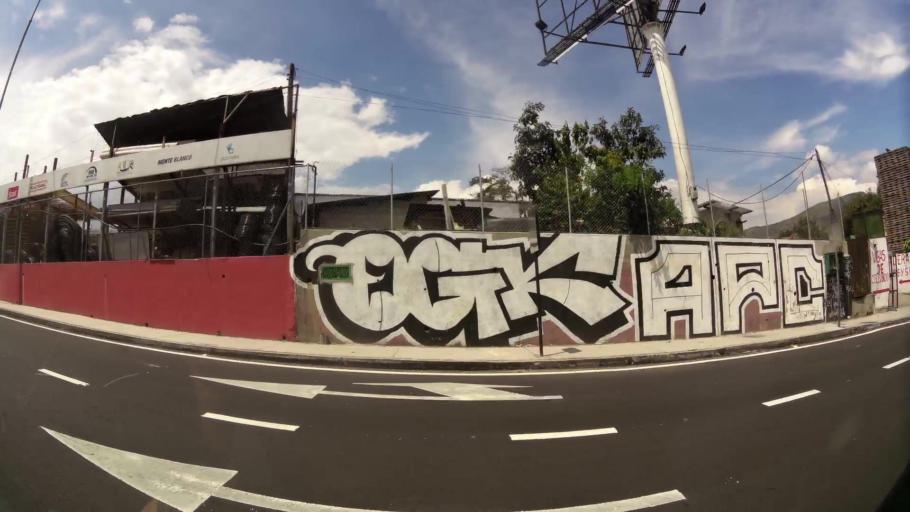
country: EC
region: Pichincha
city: Sangolqui
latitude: -0.2143
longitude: -78.3897
